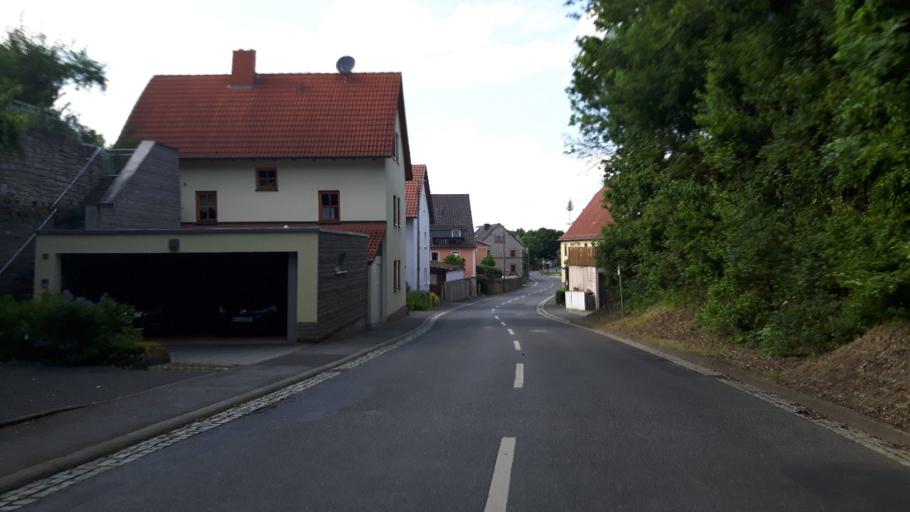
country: DE
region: Bavaria
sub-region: Regierungsbezirk Unterfranken
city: Reichenberg
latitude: 49.7090
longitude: 9.9300
